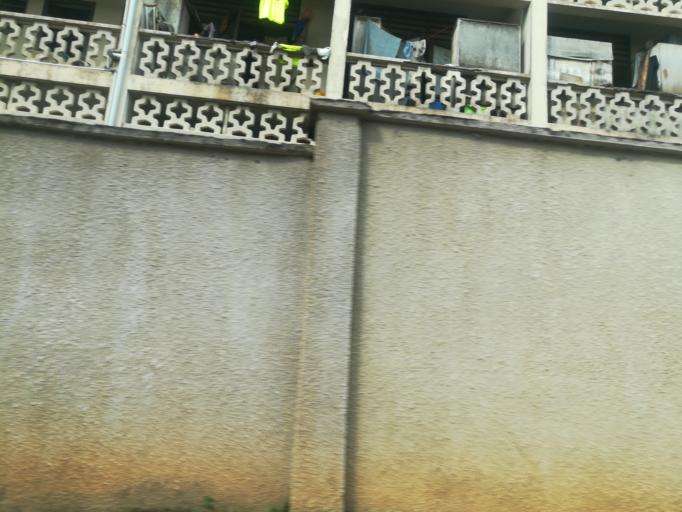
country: NG
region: Oyo
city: Ibadan
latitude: 7.4453
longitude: 3.8982
